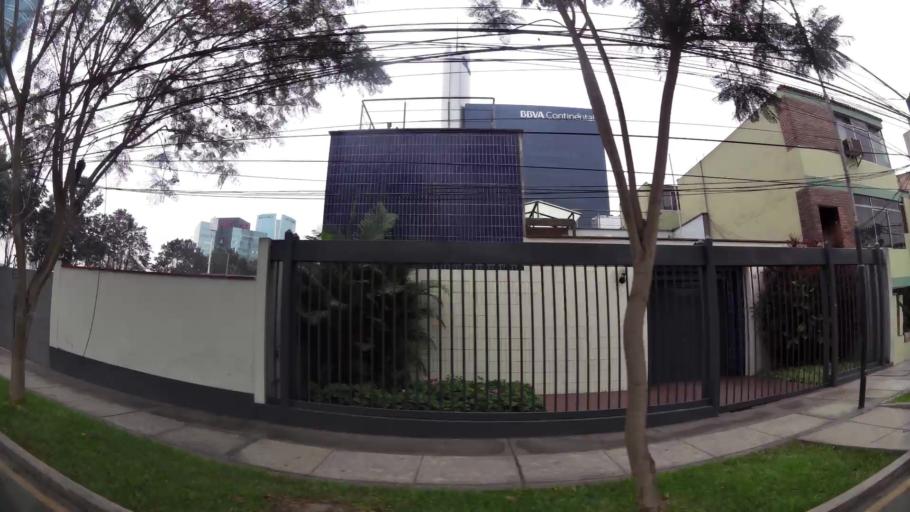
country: PE
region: Lima
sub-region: Lima
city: San Luis
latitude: -12.0950
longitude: -77.0208
